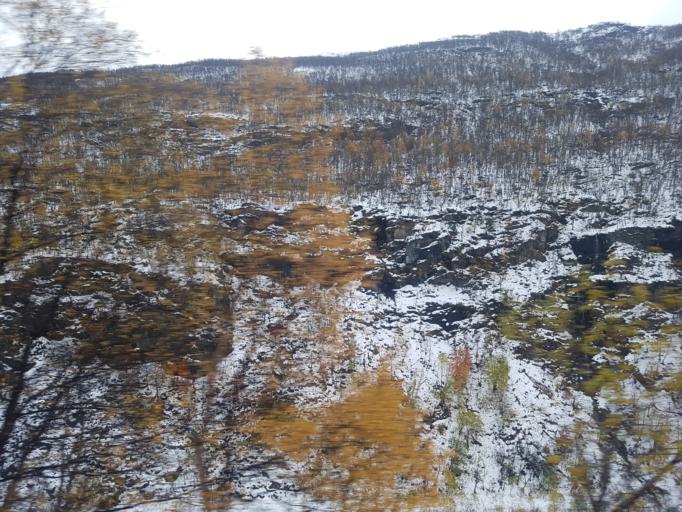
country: NO
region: Sor-Trondelag
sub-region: Oppdal
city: Oppdal
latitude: 62.3575
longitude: 9.6308
